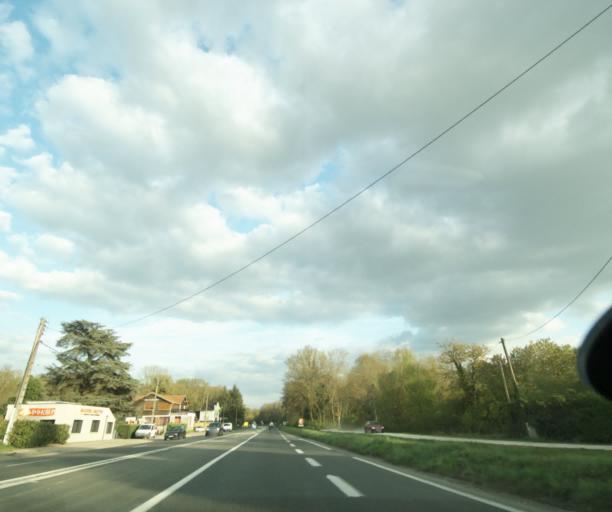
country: FR
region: Ile-de-France
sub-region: Departement de Seine-et-Marne
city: Chailly-en-Biere
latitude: 48.4535
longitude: 2.6209
